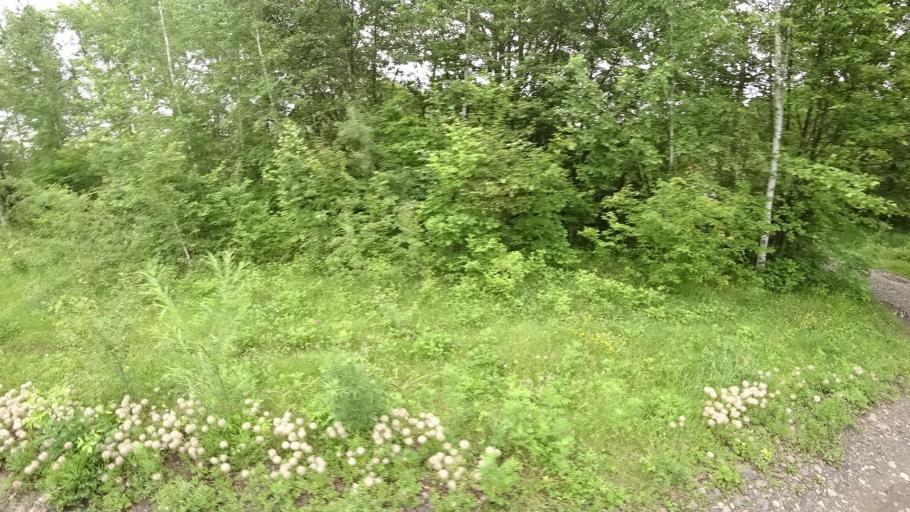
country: RU
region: Khabarovsk Krai
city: Amursk
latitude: 49.9049
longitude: 136.1326
